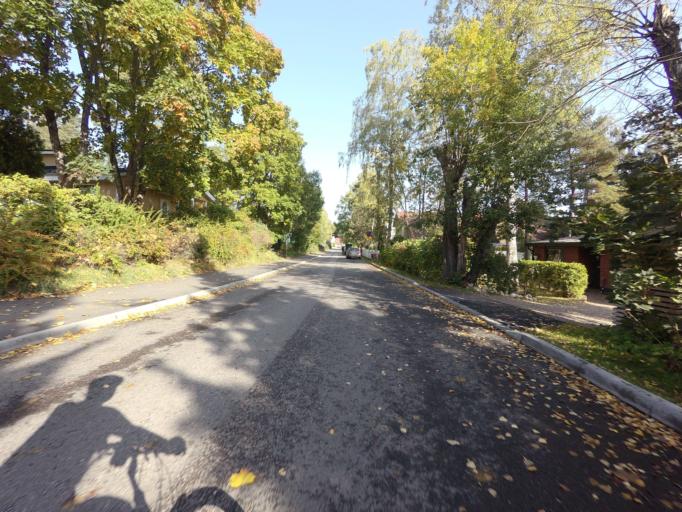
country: FI
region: Uusimaa
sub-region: Helsinki
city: Espoo
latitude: 60.1799
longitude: 24.6558
